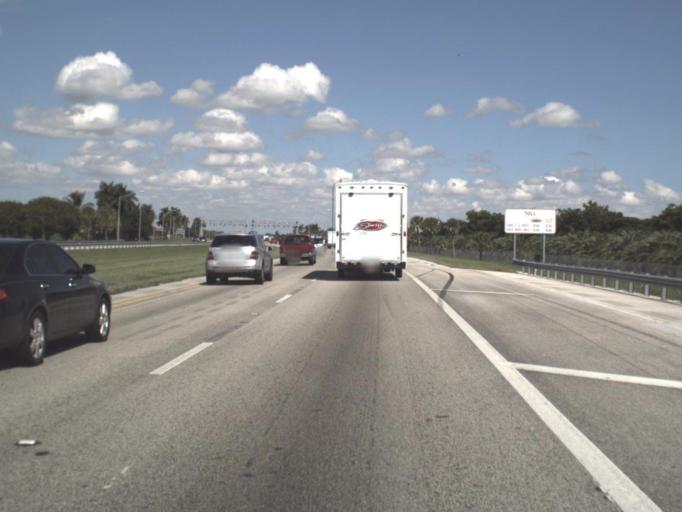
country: US
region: Florida
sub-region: Miami-Dade County
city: Goulds
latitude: 25.5441
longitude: -80.3627
